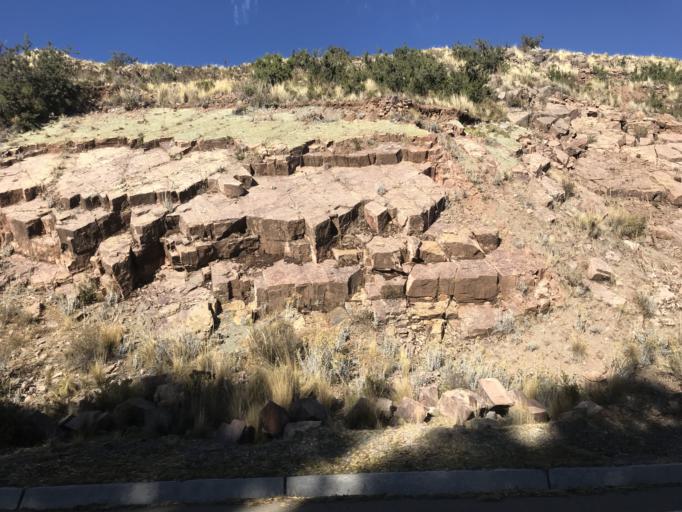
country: BO
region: La Paz
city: San Pedro
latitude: -16.1895
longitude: -68.9260
